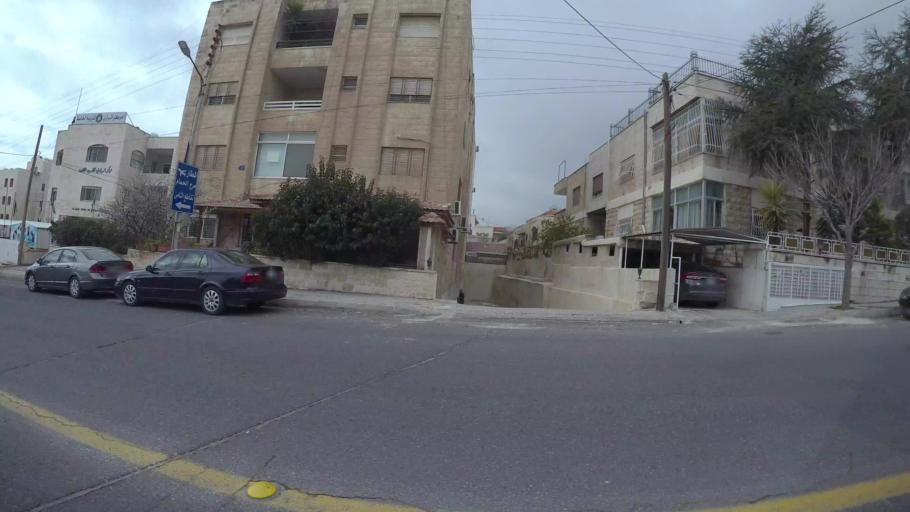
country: JO
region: Amman
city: Wadi as Sir
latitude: 31.9653
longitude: 35.8527
